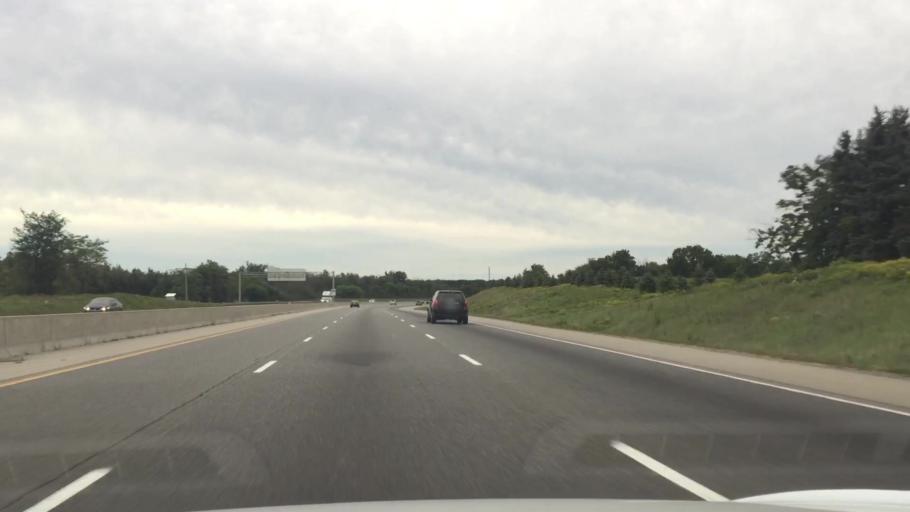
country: CA
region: Ontario
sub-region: Oxford County
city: Woodstock
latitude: 43.2183
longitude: -80.6053
